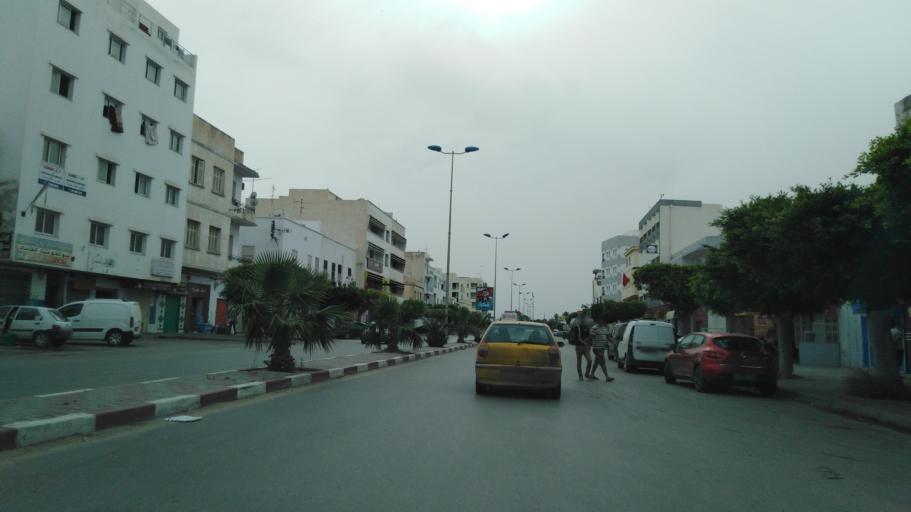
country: TN
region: Safaqis
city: Sfax
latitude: 34.7333
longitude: 10.7545
